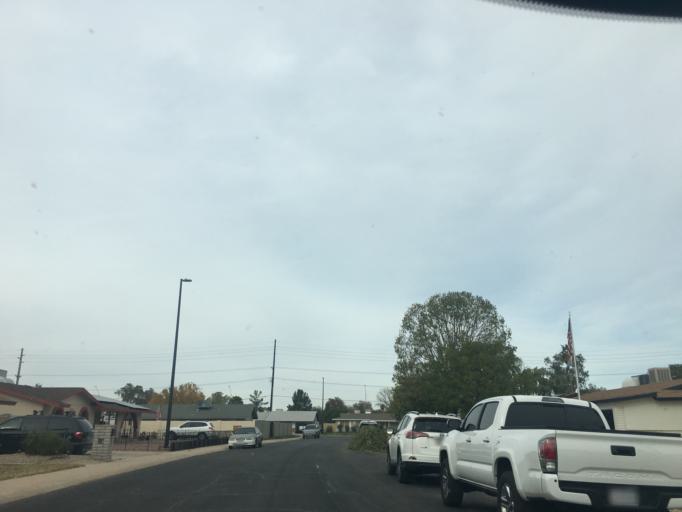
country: US
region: Arizona
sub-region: Maricopa County
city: Gilbert
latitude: 33.3630
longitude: -111.7970
